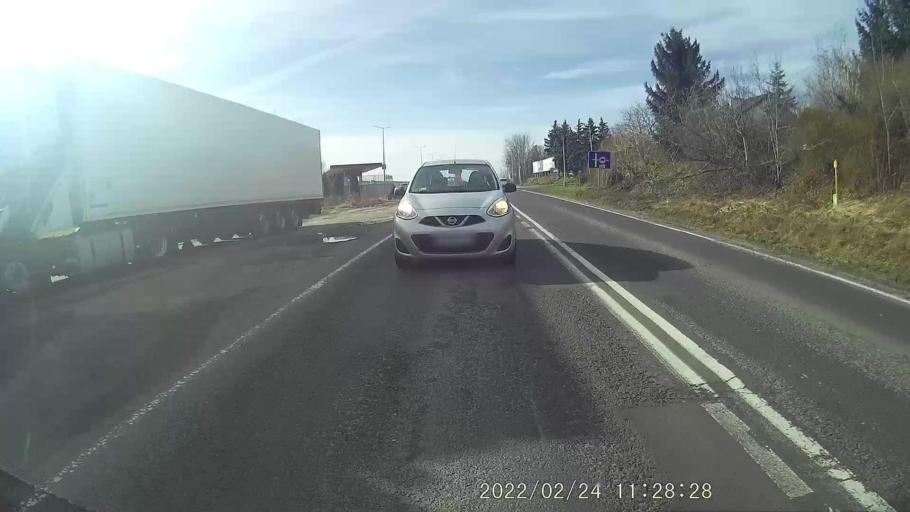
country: PL
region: Lower Silesian Voivodeship
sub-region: Powiat polkowicki
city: Przemkow
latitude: 51.5325
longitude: 15.6848
